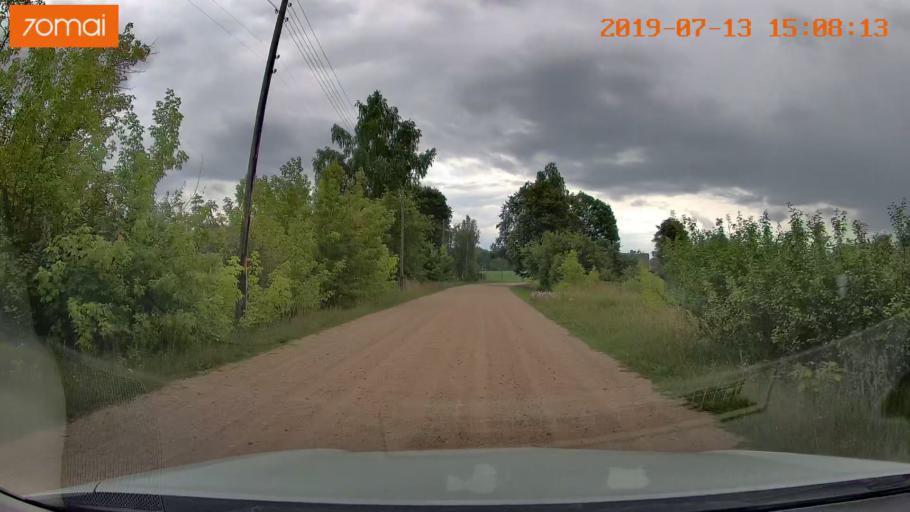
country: BY
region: Mogilev
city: Hlusha
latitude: 53.1810
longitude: 28.7574
